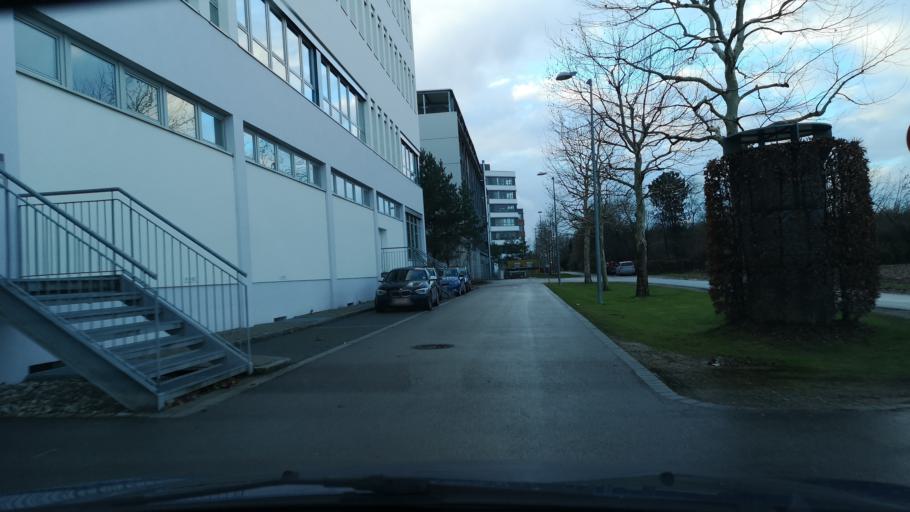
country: DE
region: Bavaria
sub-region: Upper Bavaria
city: Garching bei Munchen
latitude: 48.2526
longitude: 11.6353
